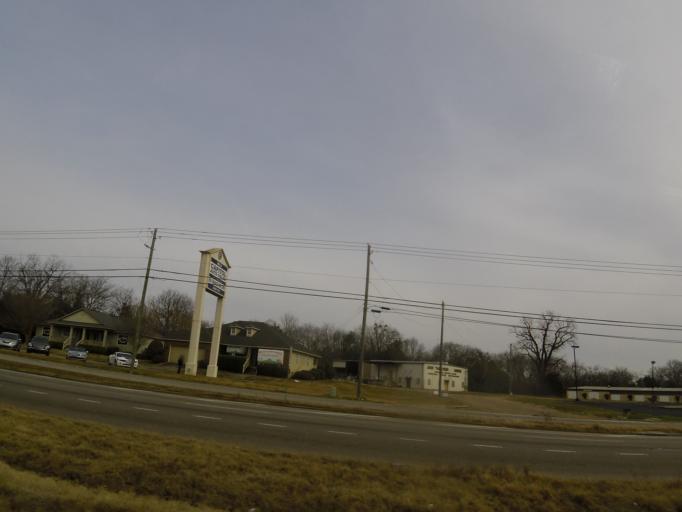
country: US
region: Alabama
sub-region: Montgomery County
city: Montgomery
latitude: 32.3226
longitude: -86.2373
